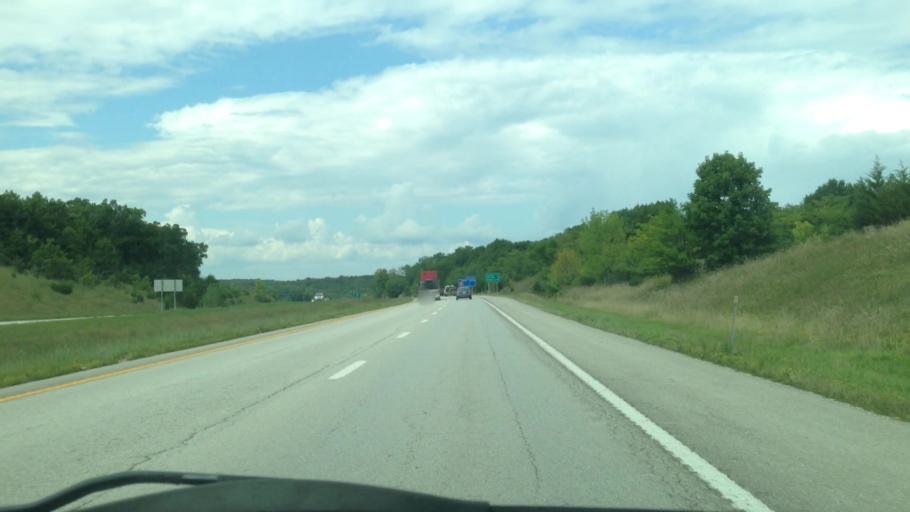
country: US
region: Missouri
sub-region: Pike County
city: Bowling Green
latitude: 39.3441
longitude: -91.1838
